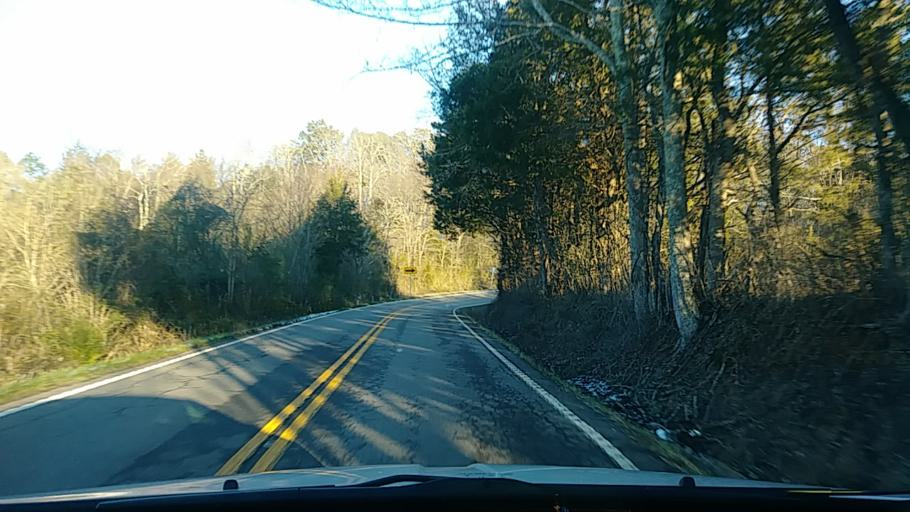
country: US
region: Tennessee
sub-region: Greene County
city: Mosheim
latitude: 36.1276
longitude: -83.1075
